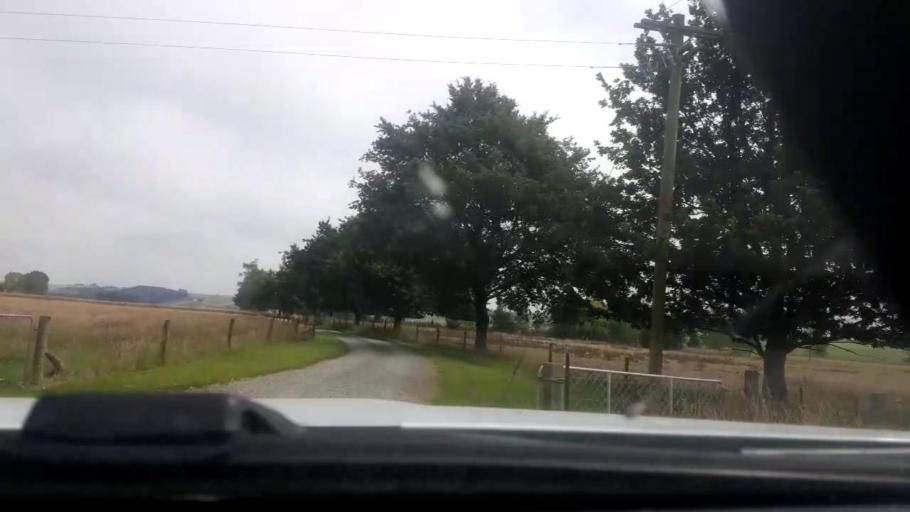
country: NZ
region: Canterbury
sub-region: Timaru District
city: Pleasant Point
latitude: -44.3230
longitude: 171.1931
